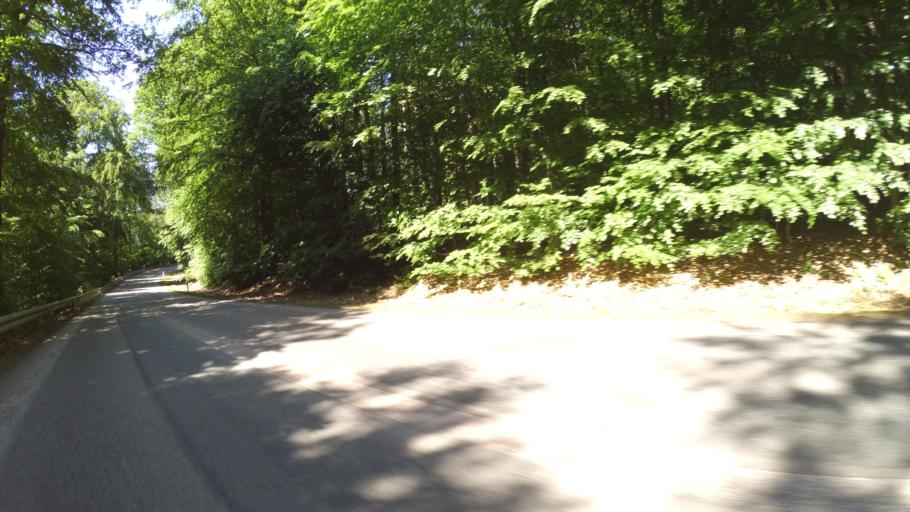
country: DE
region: Saarland
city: Quierschied
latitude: 49.3269
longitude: 7.0057
